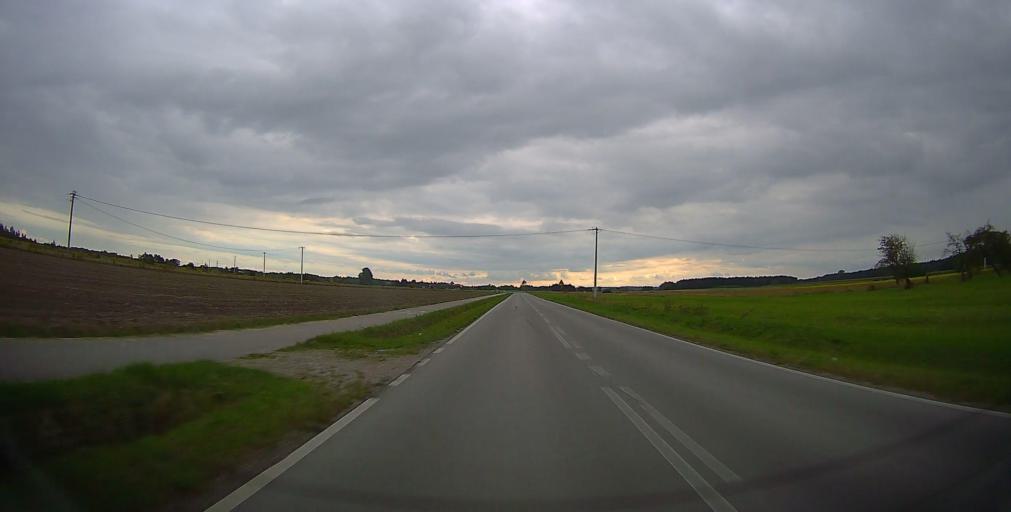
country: PL
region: Masovian Voivodeship
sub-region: Powiat radomski
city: Zakrzew
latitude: 51.4448
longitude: 21.0549
